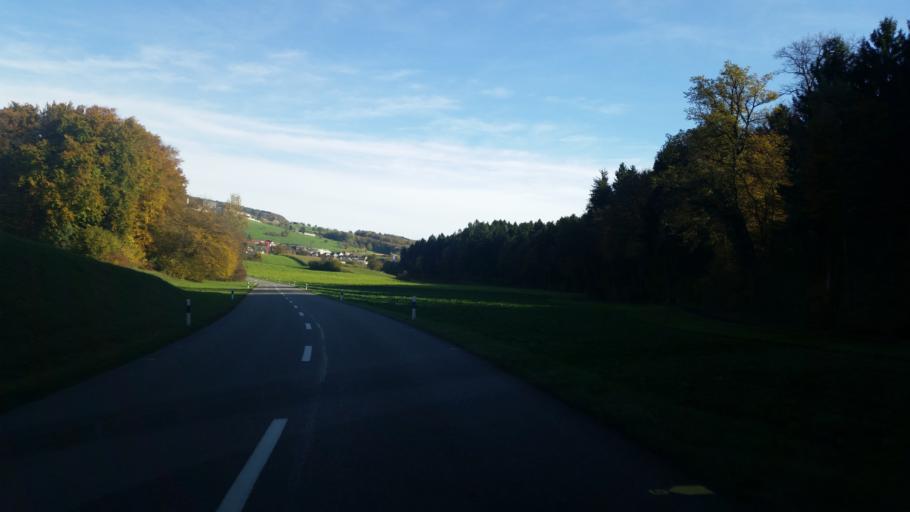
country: CH
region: Aargau
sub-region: Bezirk Baden
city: Kunten
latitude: 47.3945
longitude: 8.3178
